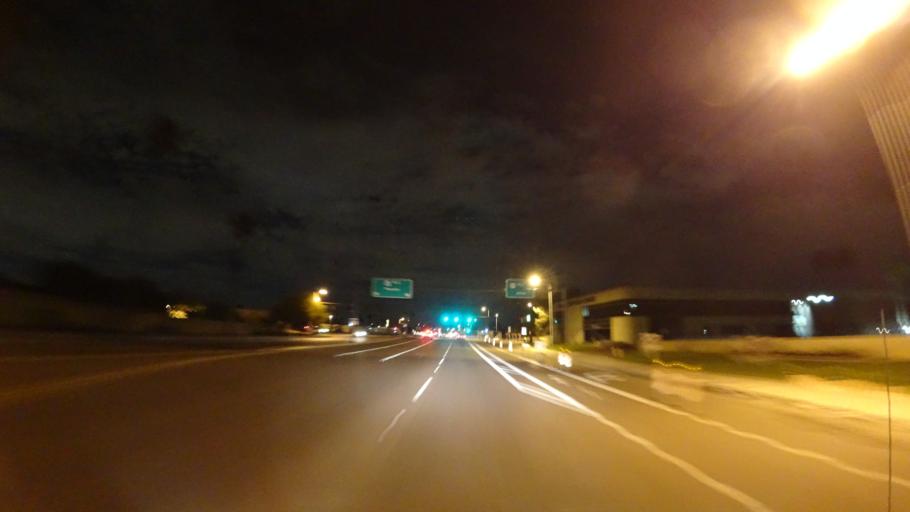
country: US
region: Arizona
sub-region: Maricopa County
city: Tempe
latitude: 33.3842
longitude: -111.9091
